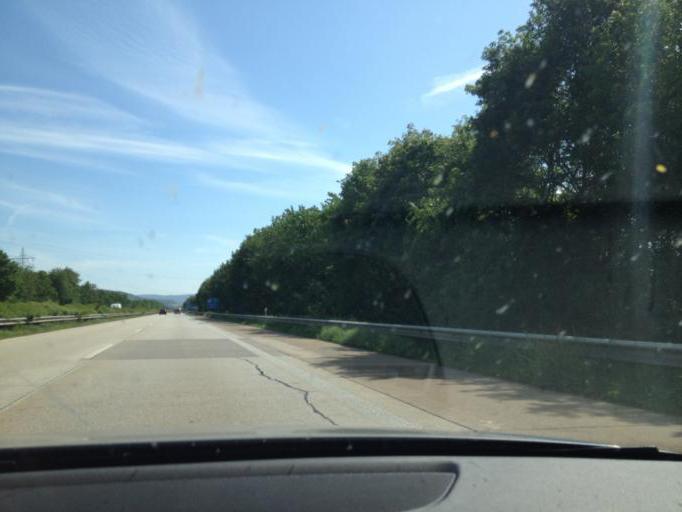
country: DE
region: Rheinland-Pfalz
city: Esch
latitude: 49.9141
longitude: 6.8550
